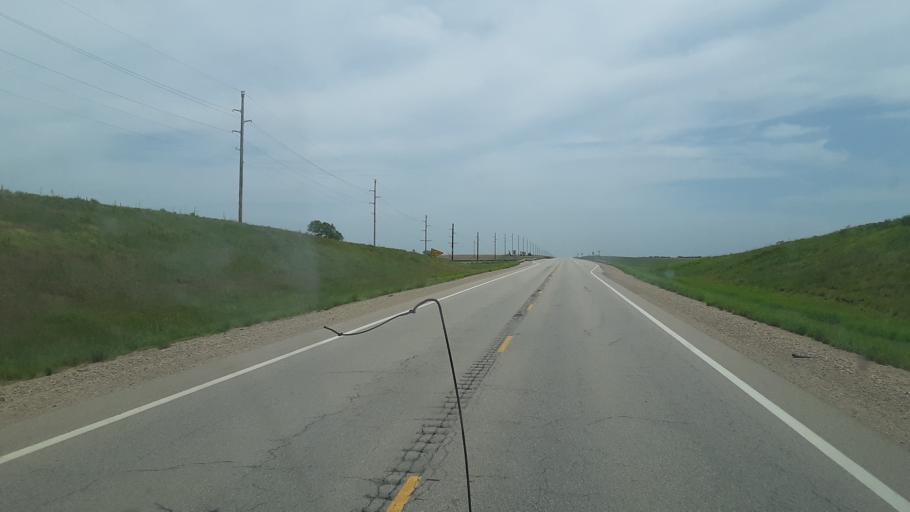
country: US
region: Kansas
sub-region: Greenwood County
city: Eureka
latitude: 37.8371
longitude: -96.0341
